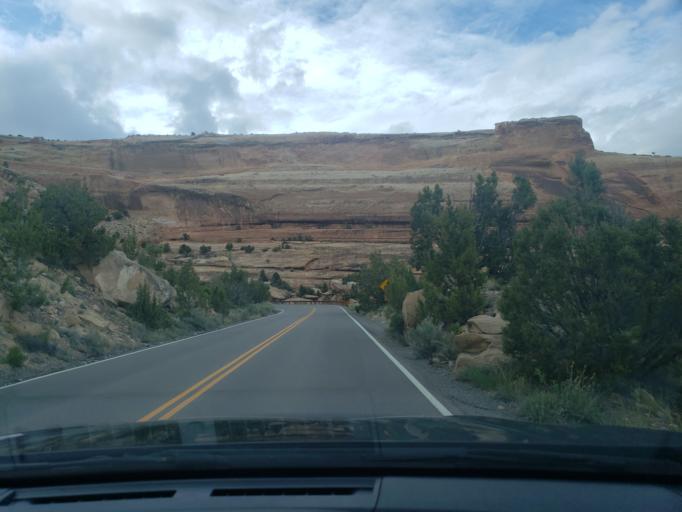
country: US
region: Colorado
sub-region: Mesa County
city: Redlands
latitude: 39.0298
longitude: -108.6453
